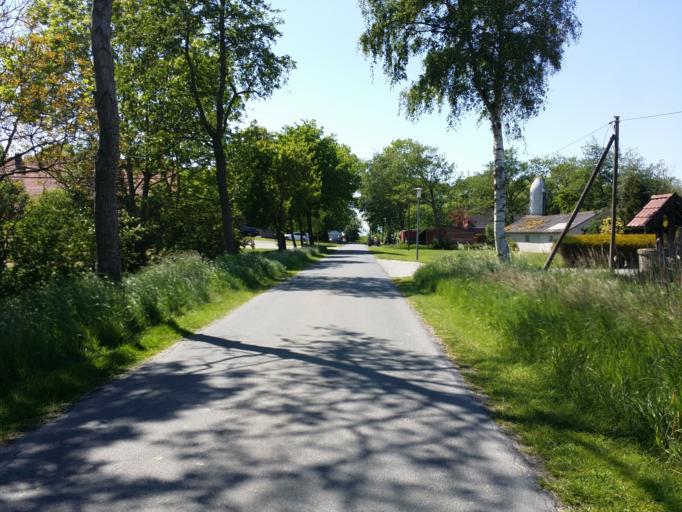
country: DE
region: Lower Saxony
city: Esens
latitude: 53.6747
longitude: 7.6354
